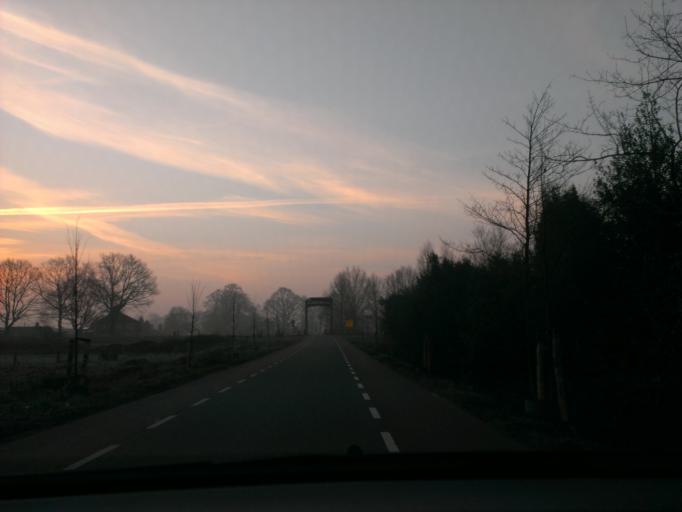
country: NL
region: Gelderland
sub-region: Gemeente Heerde
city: Heerde
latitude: 52.3781
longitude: 6.0453
